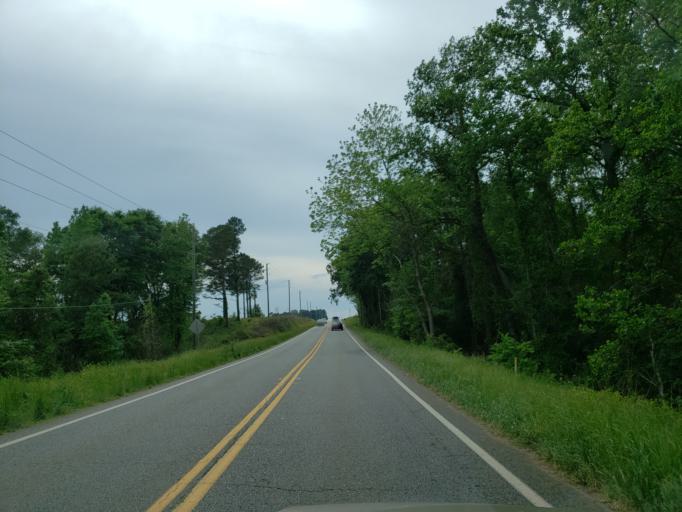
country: US
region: Georgia
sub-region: Macon County
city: Marshallville
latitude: 32.3664
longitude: -83.9065
